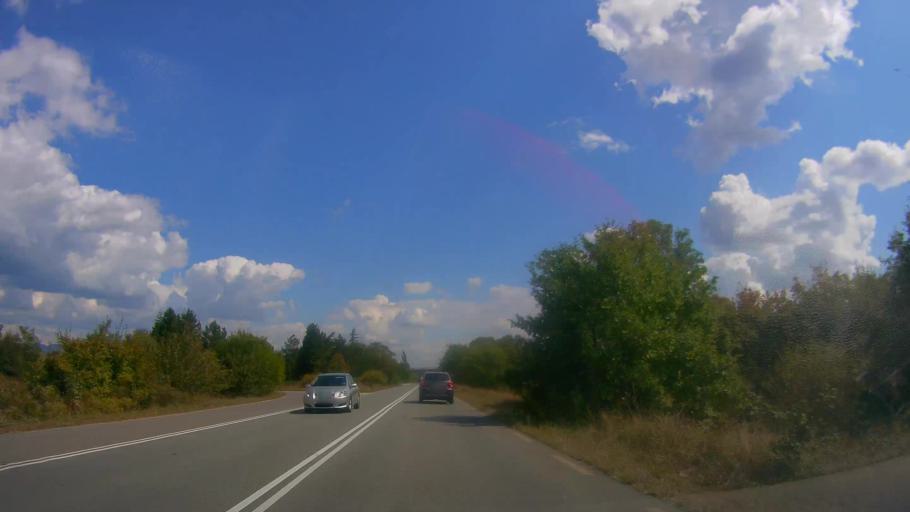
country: BG
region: Sliven
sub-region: Obshtina Tvurditsa
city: Tvurditsa
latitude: 42.6524
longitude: 25.9702
